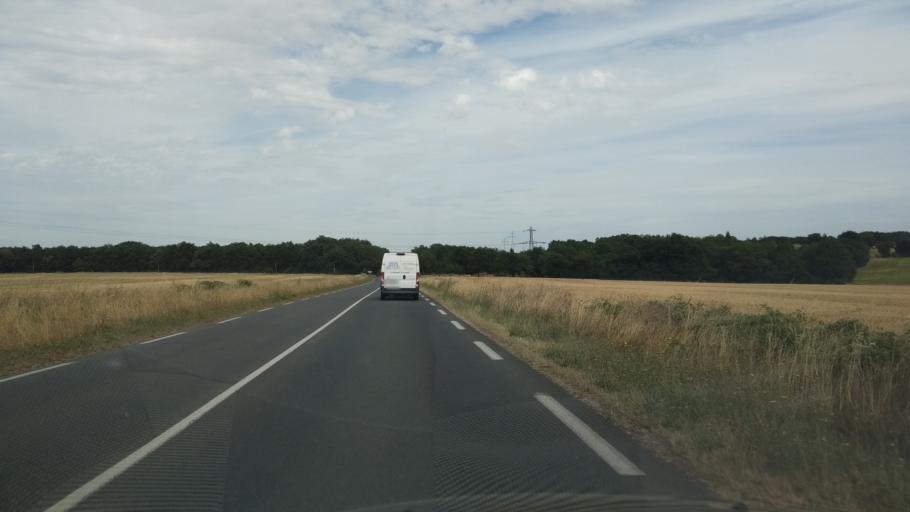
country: FR
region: Poitou-Charentes
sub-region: Departement de la Vienne
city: Bonnes
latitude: 46.5660
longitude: 0.6028
